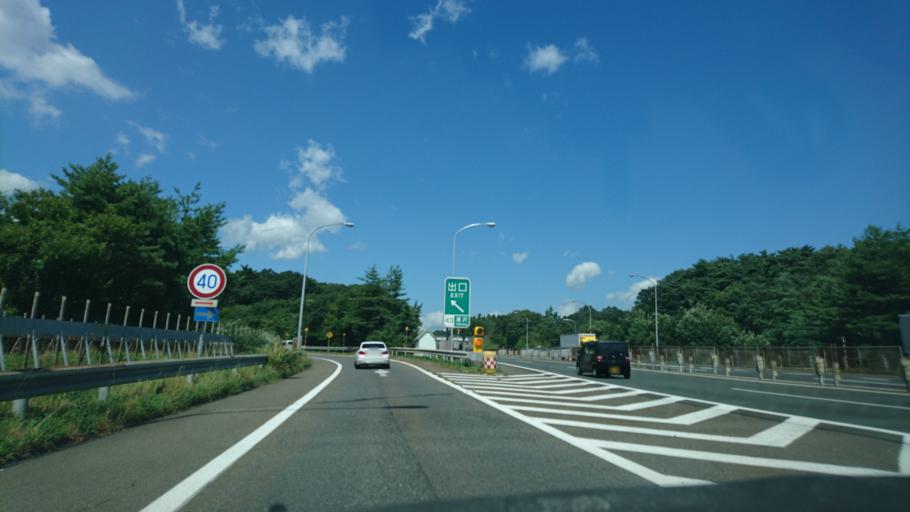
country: JP
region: Iwate
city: Morioka-shi
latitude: 39.7952
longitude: 141.1121
